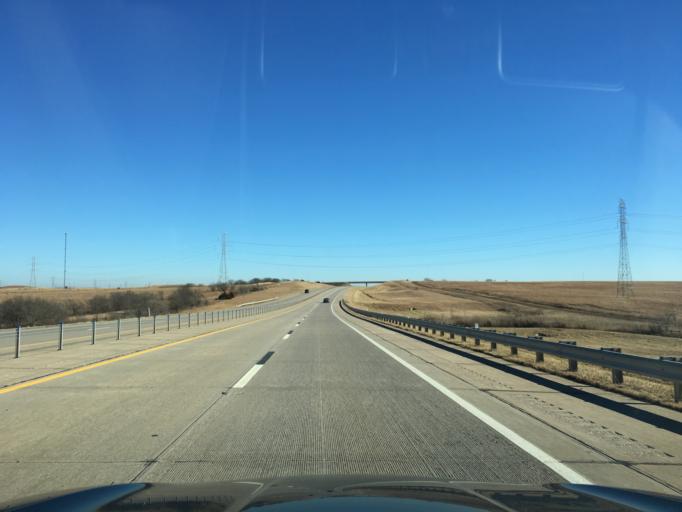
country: US
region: Oklahoma
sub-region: Noble County
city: Perry
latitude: 36.3921
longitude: -97.1122
